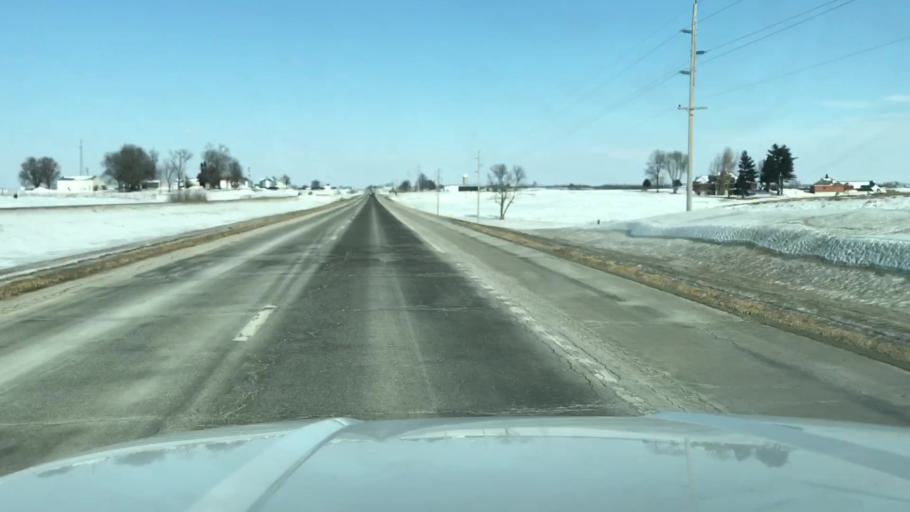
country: US
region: Missouri
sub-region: Nodaway County
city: Maryville
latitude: 40.2362
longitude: -94.8675
